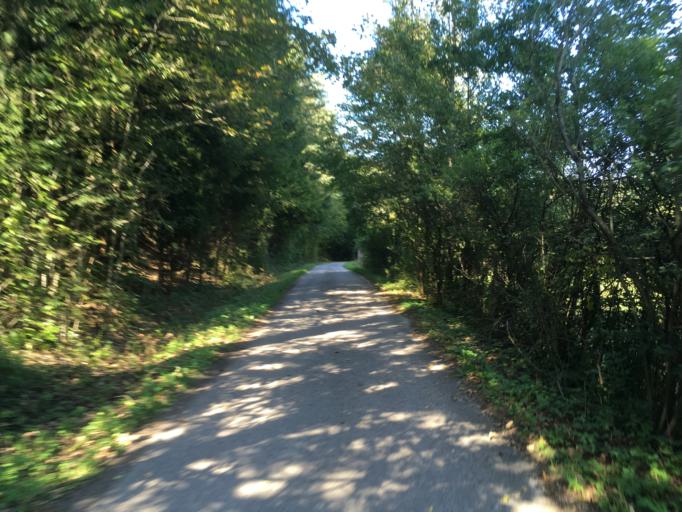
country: SK
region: Trenciansky
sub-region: Okres Povazska Bystrica
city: Povazska Bystrica
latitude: 49.0188
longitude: 18.4397
